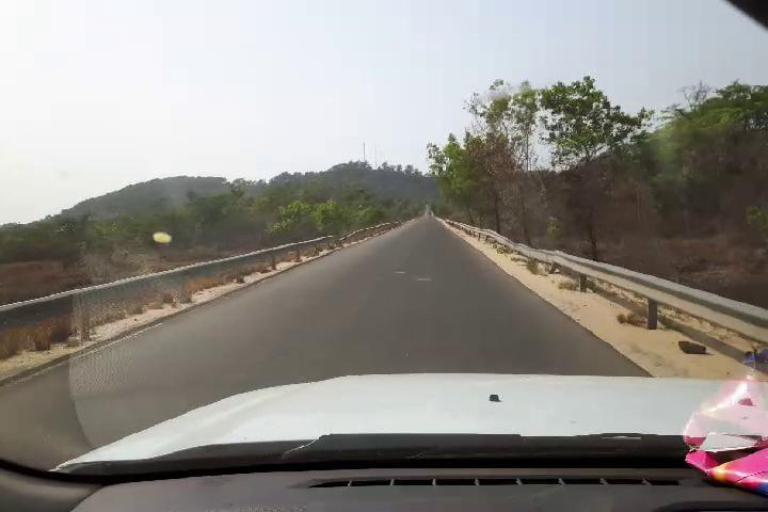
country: SL
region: Western Area
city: Waterloo
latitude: 8.2567
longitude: -13.1584
